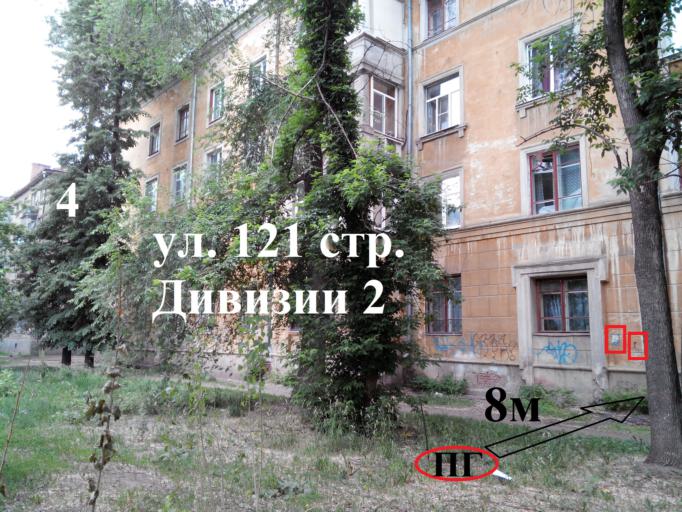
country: RU
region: Voronezj
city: Voronezh
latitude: 51.6469
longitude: 39.1688
